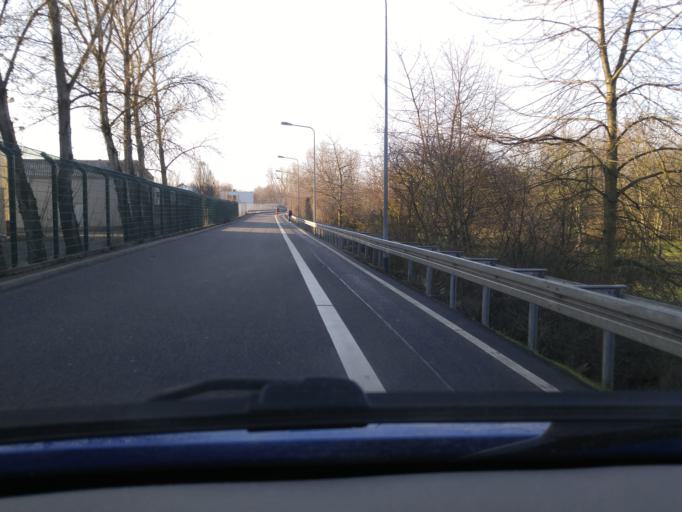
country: DE
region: Hesse
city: Niederrad
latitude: 50.0945
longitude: 8.5804
